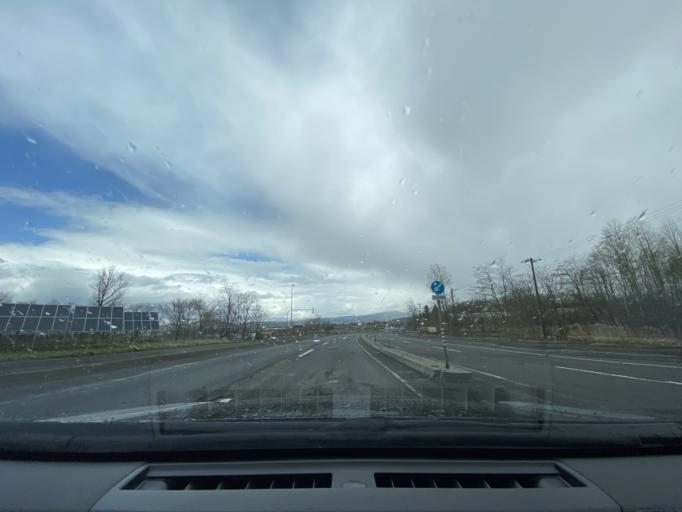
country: JP
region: Hokkaido
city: Fukagawa
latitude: 43.6932
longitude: 142.0580
